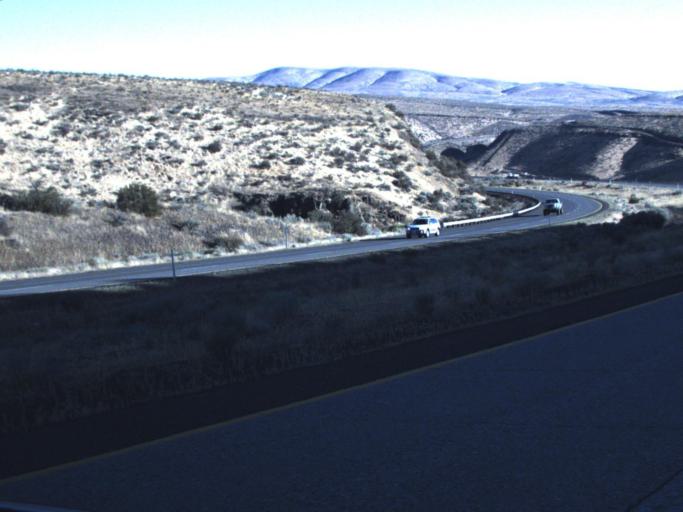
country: US
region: Washington
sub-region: Kittitas County
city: Kittitas
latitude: 46.7916
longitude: -120.3591
